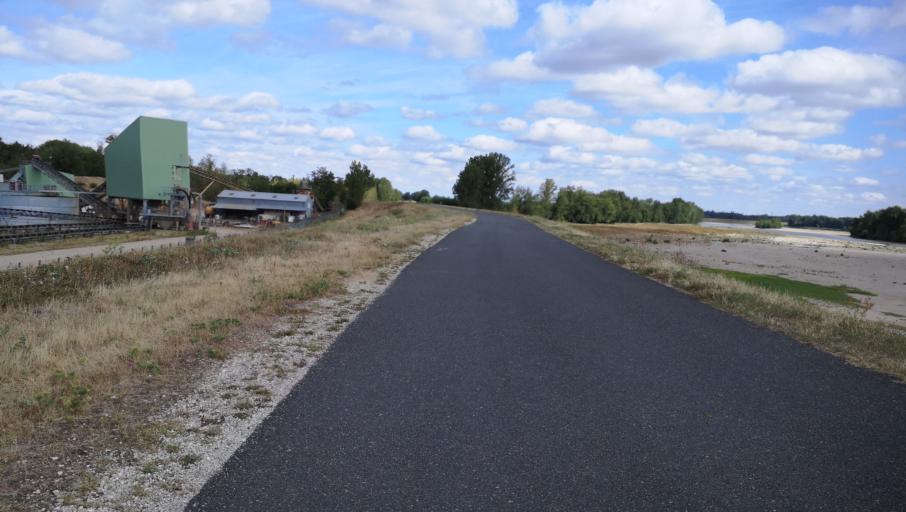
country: FR
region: Centre
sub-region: Departement du Loiret
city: Sandillon
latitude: 47.8638
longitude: 2.0285
